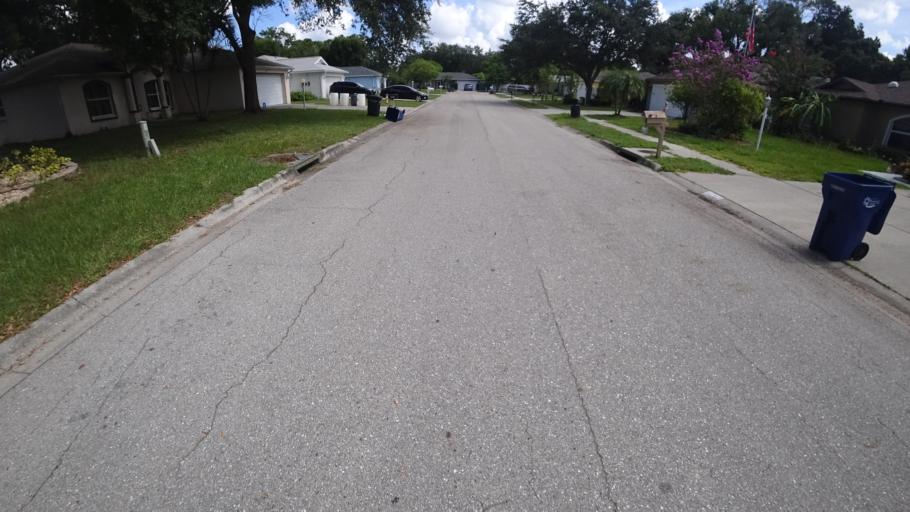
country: US
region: Florida
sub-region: Manatee County
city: Samoset
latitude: 27.4500
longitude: -82.5400
